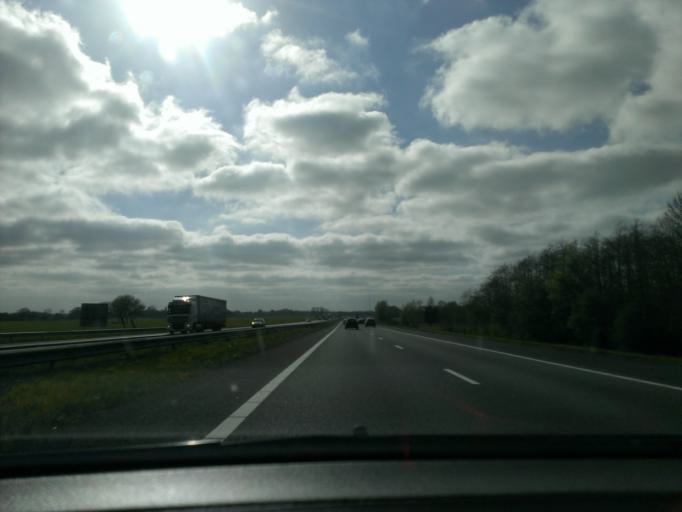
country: NL
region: Drenthe
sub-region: Gemeente De Wolden
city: Ruinen
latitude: 52.6766
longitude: 6.3346
